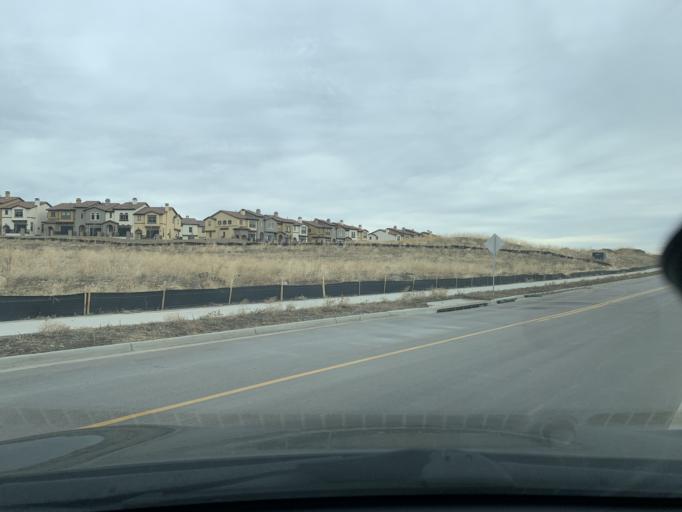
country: US
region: Colorado
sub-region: Jefferson County
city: West Pleasant View
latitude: 39.6675
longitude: -105.1765
